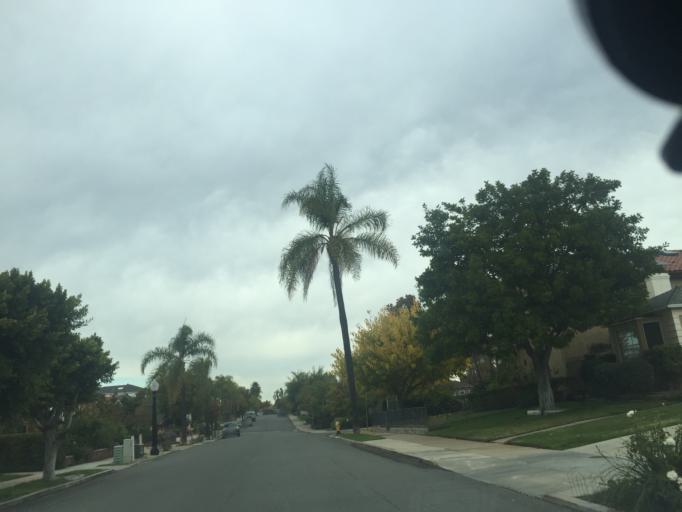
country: US
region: California
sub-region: San Diego County
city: Lemon Grove
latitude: 32.7617
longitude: -117.0935
